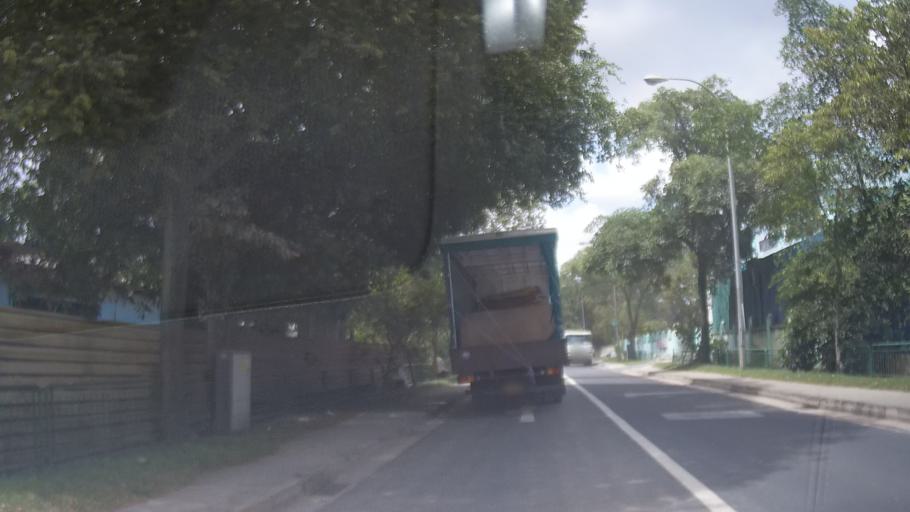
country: MY
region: Johor
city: Johor Bahru
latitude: 1.4290
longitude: 103.7488
